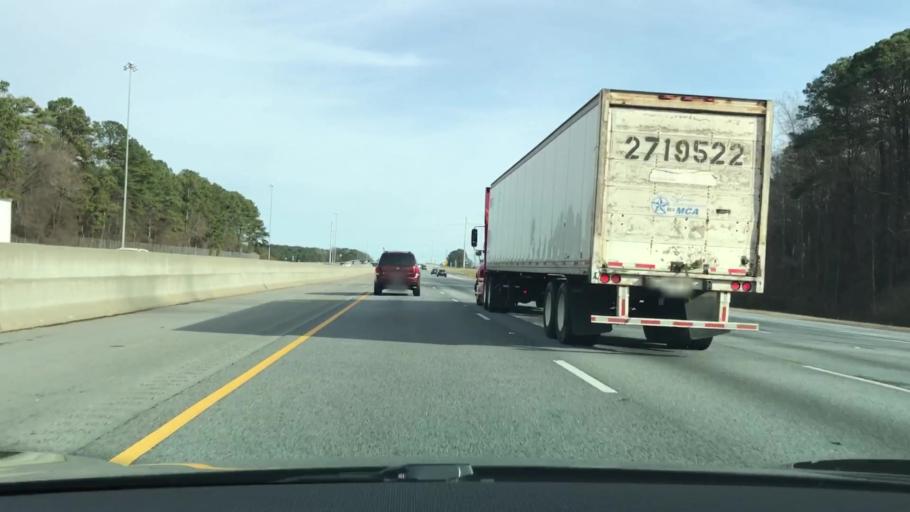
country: US
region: Georgia
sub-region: Newton County
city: Oxford
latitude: 33.6152
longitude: -83.8511
